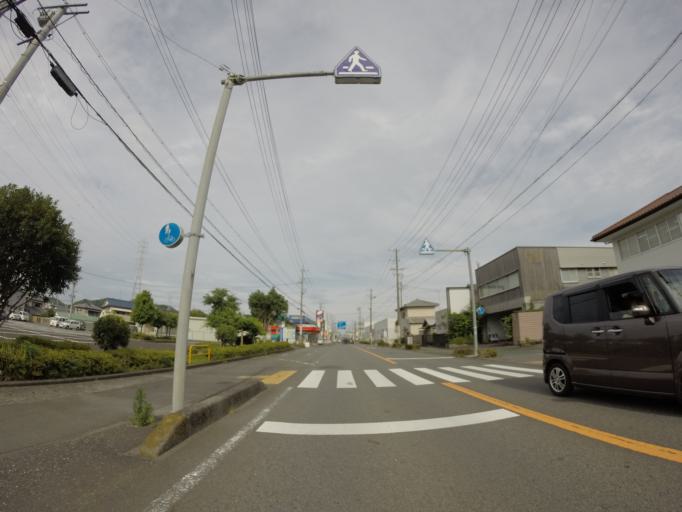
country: JP
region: Shizuoka
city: Shimada
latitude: 34.8387
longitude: 138.1737
